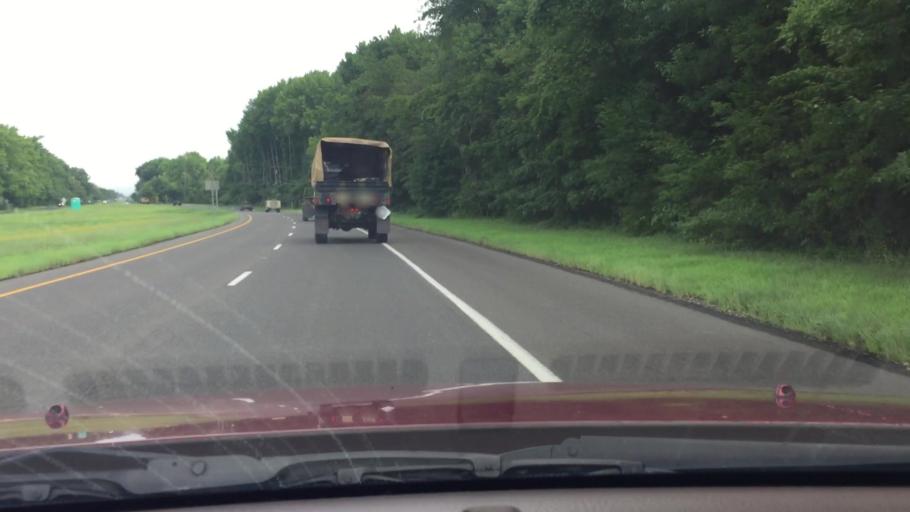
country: US
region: New Jersey
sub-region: Burlington County
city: Fort Dix
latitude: 40.0713
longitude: -74.6559
